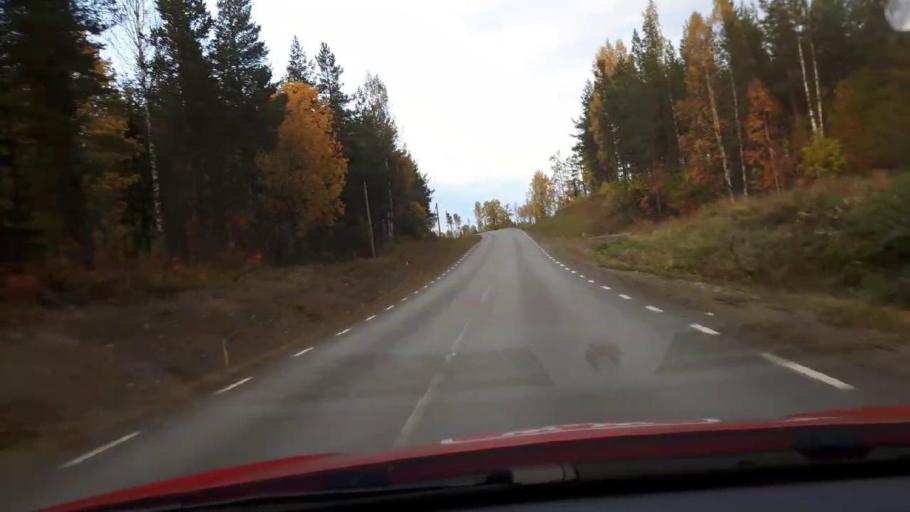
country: SE
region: Jaemtland
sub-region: OEstersunds Kommun
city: Lit
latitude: 63.3145
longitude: 15.1412
